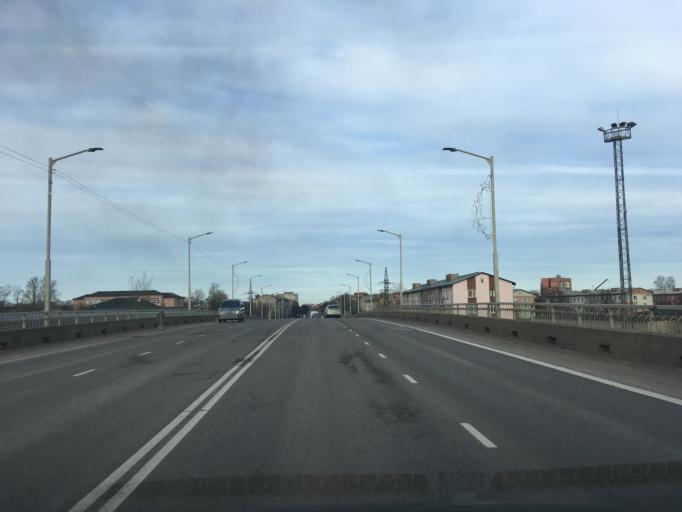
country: EE
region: Ida-Virumaa
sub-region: Narva linn
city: Narva
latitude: 59.3716
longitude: 28.1840
